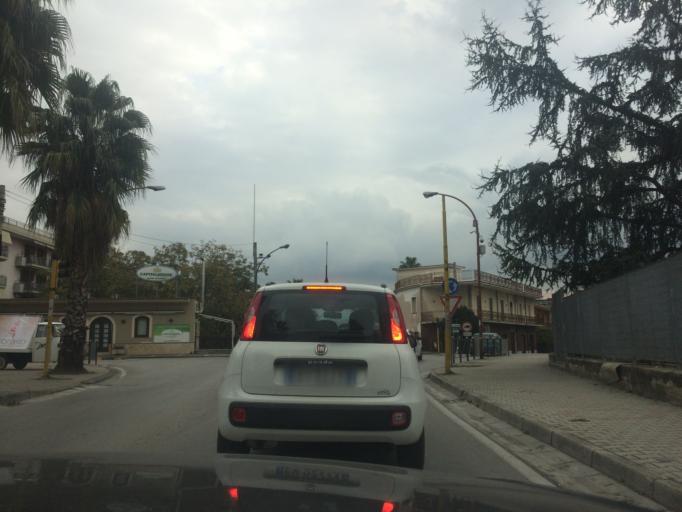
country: IT
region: Campania
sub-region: Provincia di Napoli
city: Palma Campania
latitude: 40.8684
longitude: 14.5476
